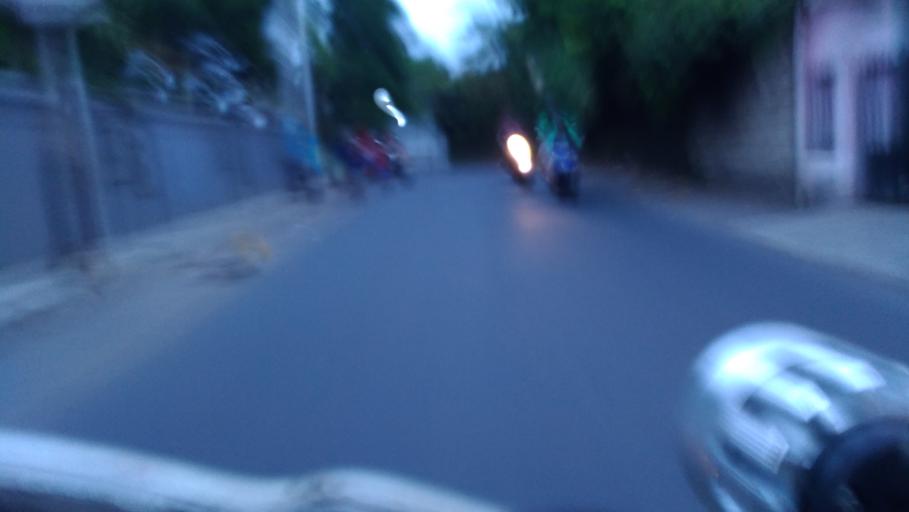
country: ID
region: West Java
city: Depok
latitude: -6.3568
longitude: 106.8805
